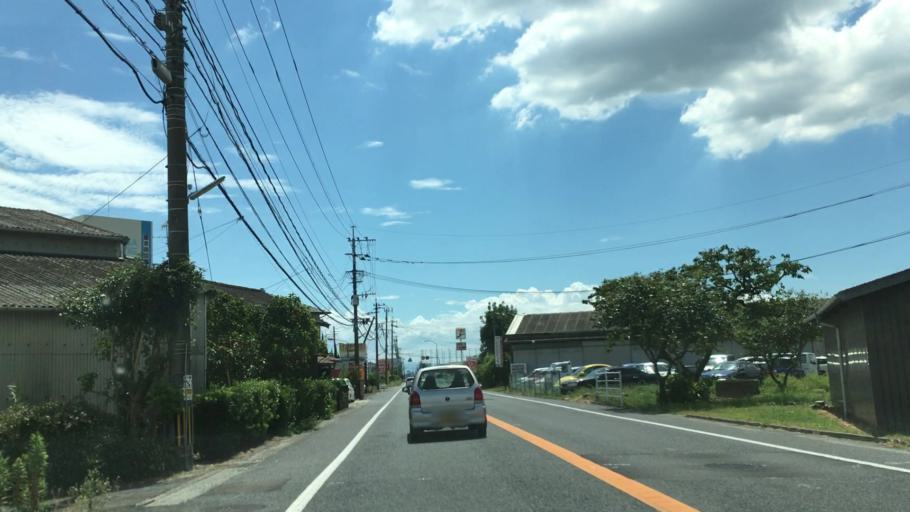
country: JP
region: Saga Prefecture
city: Kanzakimachi-kanzaki
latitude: 33.2832
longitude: 130.3459
